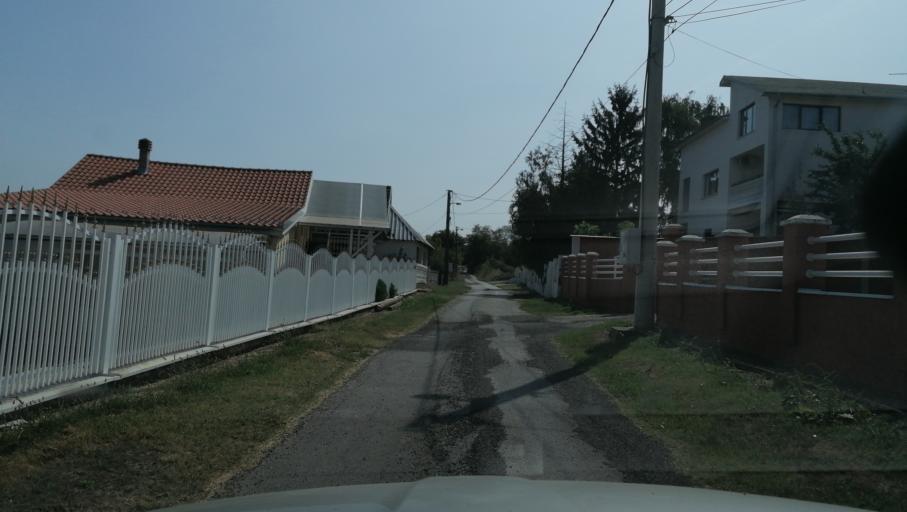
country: RS
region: Central Serbia
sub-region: Belgrade
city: Zvezdara
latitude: 44.6914
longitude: 20.5547
